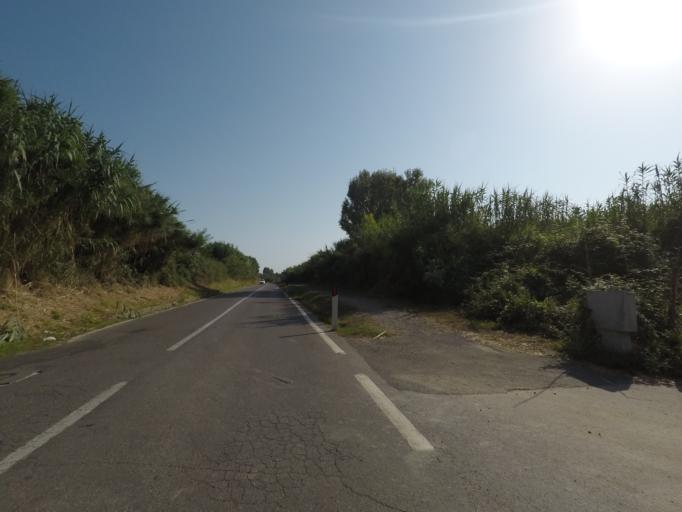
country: IT
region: Liguria
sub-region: Provincia di La Spezia
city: Casano-Dogana-Isola
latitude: 44.0578
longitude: 10.0274
